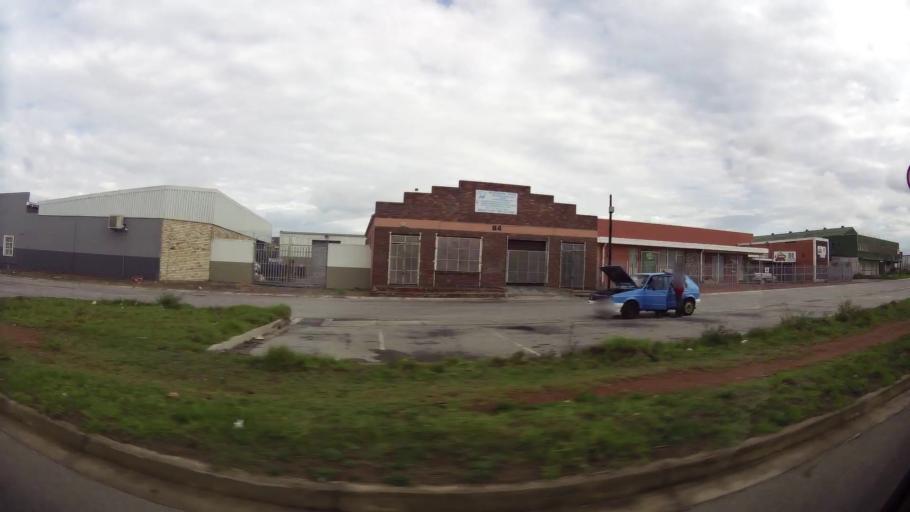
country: ZA
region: Eastern Cape
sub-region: Nelson Mandela Bay Metropolitan Municipality
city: Port Elizabeth
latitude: -33.9296
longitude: 25.5841
